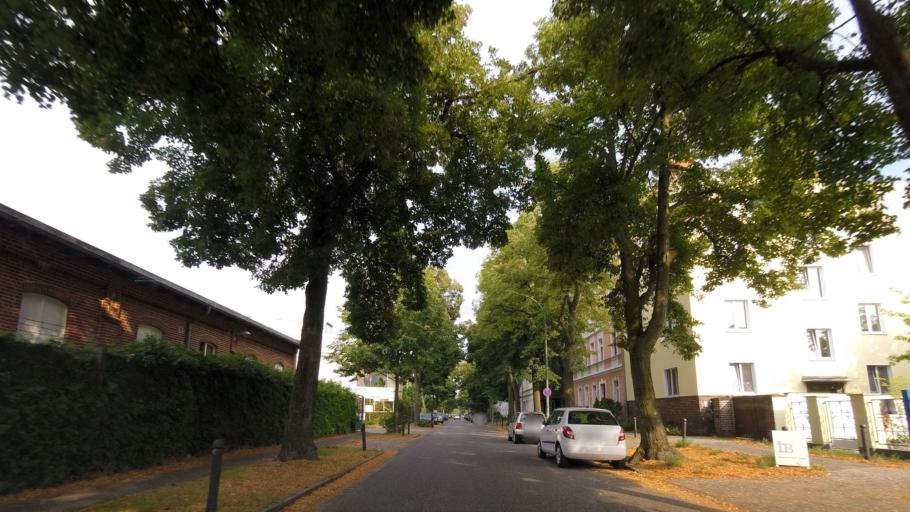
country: DE
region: Brandenburg
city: Potsdam
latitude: 52.3844
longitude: 13.1039
